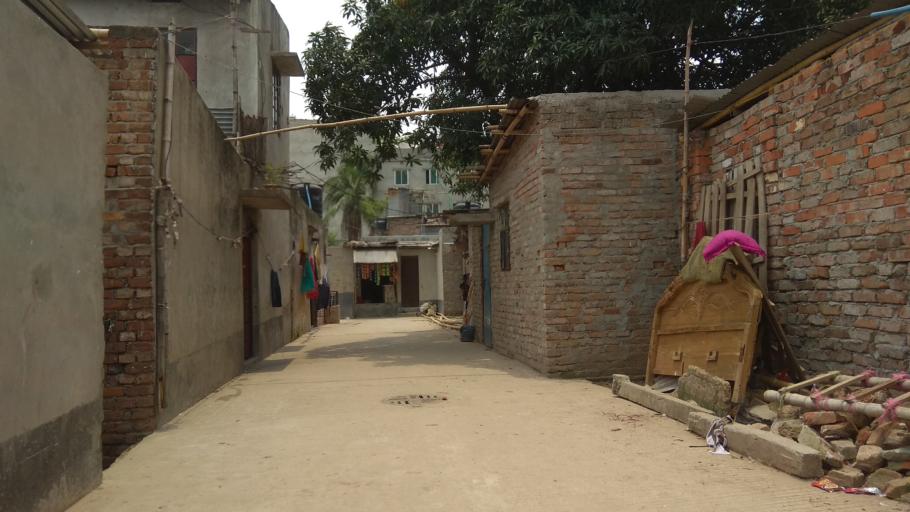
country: BD
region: Dhaka
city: Tungi
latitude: 23.8202
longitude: 90.3554
